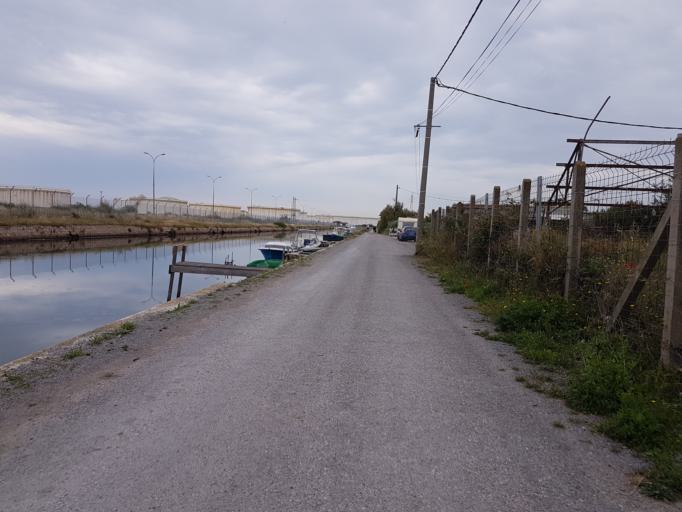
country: FR
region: Languedoc-Roussillon
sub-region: Departement de l'Herault
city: Frontignan
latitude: 43.4394
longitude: 3.7535
